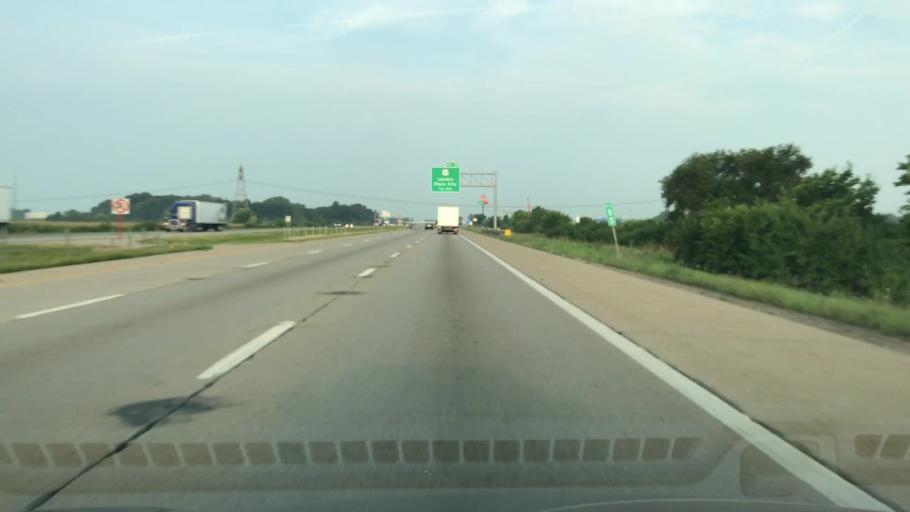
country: US
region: Ohio
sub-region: Madison County
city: West Jefferson
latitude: 39.9583
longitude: -83.3584
